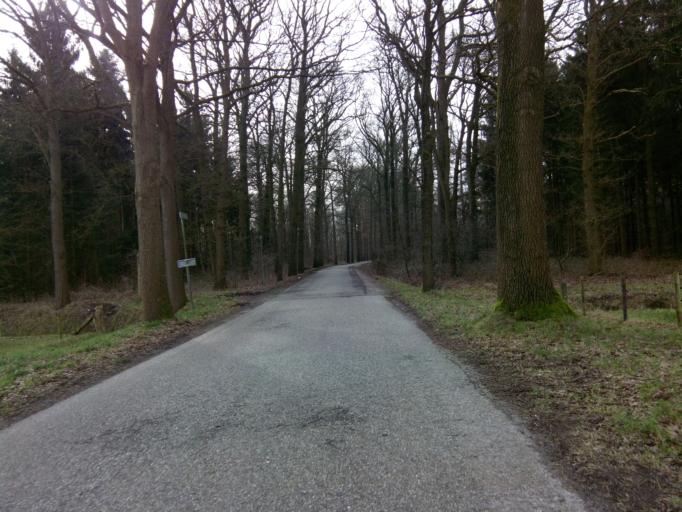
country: NL
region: Utrecht
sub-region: Gemeente Woudenberg
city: Woudenberg
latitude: 52.0902
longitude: 5.3892
